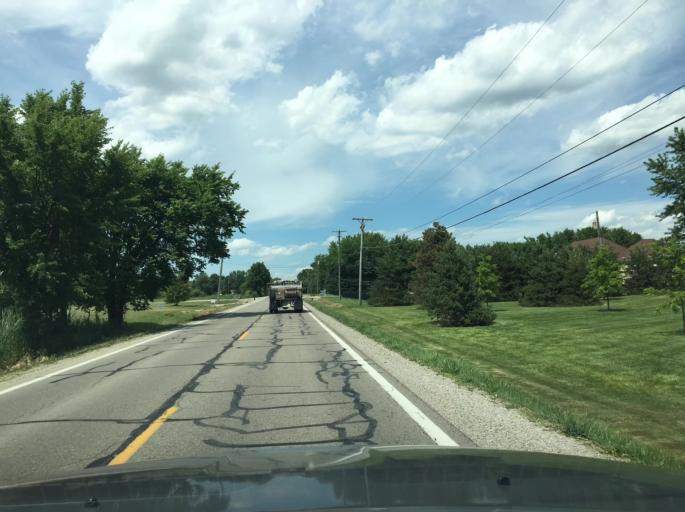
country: US
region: Michigan
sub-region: Macomb County
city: Romeo
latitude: 42.7563
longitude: -82.9609
